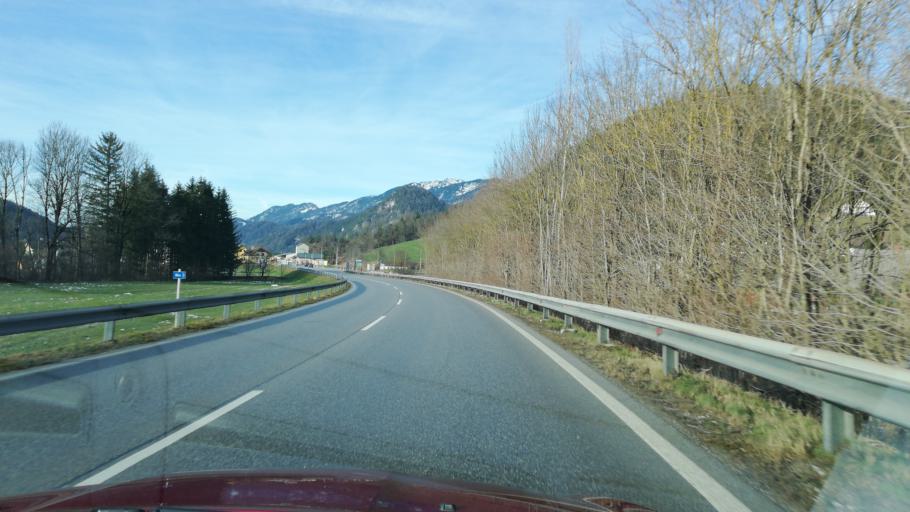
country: AT
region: Upper Austria
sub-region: Politischer Bezirk Kirchdorf an der Krems
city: Rossleithen
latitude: 47.7215
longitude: 14.3127
